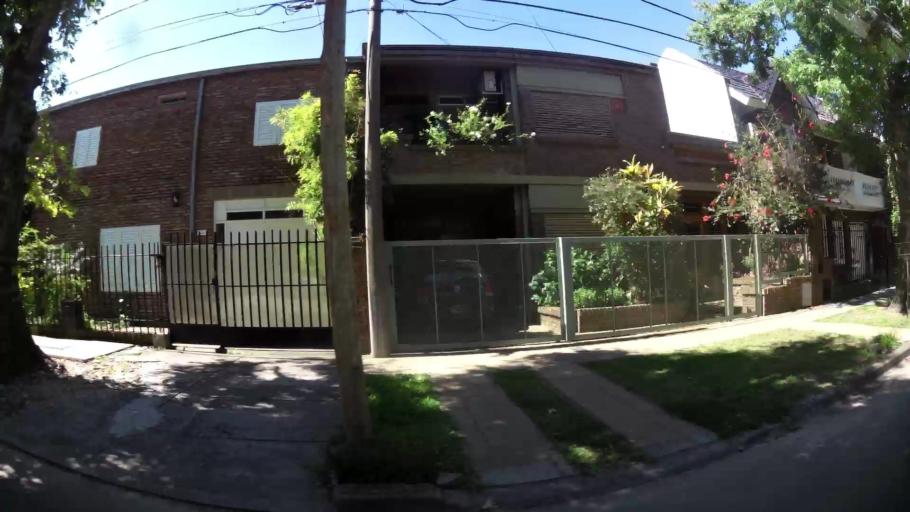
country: AR
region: Santa Fe
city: Santa Fe de la Vera Cruz
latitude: -31.6072
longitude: -60.6722
